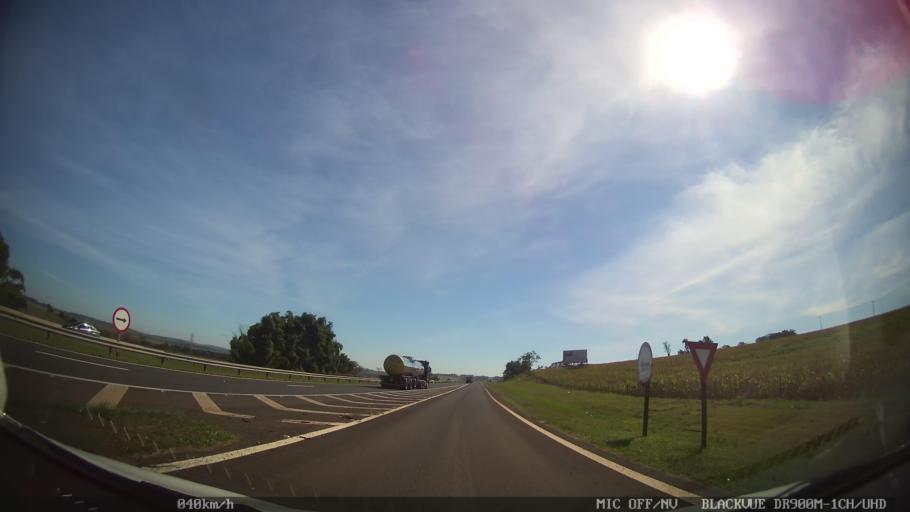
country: BR
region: Sao Paulo
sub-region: Pirassununga
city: Pirassununga
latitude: -22.0723
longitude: -47.4237
